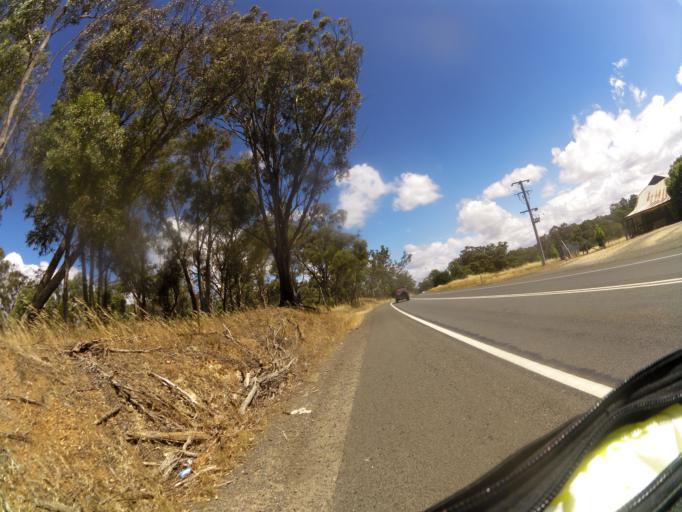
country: AU
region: Victoria
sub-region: Mount Alexander
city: Castlemaine
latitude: -37.0193
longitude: 144.2394
